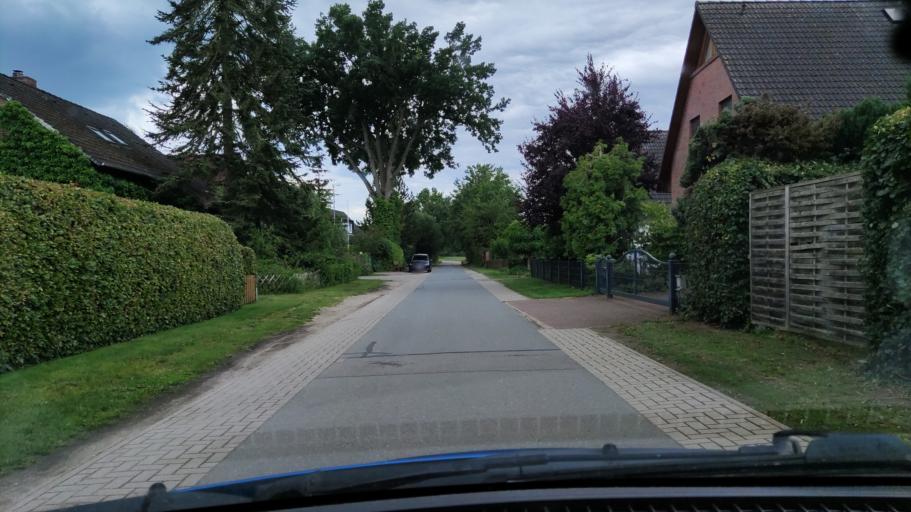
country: DE
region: Lower Saxony
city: Radbruch
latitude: 53.3096
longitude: 10.2871
